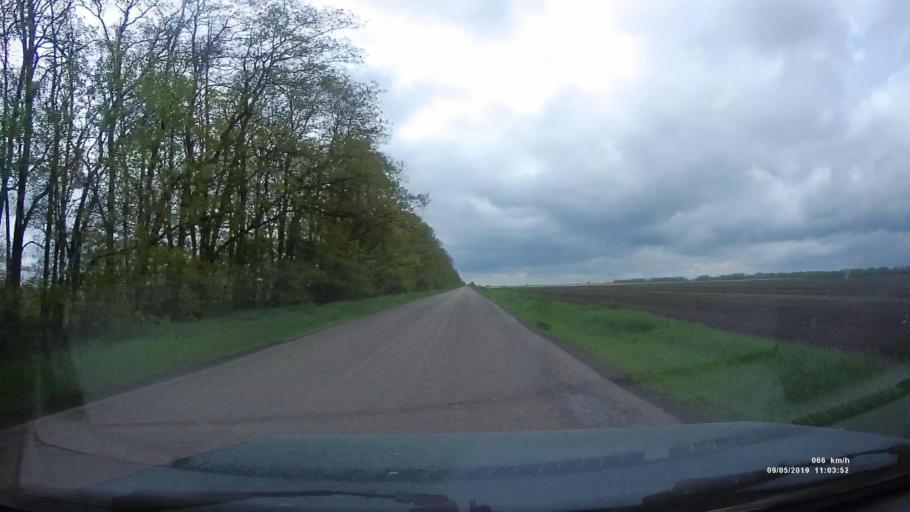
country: RU
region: Krasnodarskiy
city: Kanelovskaya
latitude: 46.8231
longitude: 39.2099
